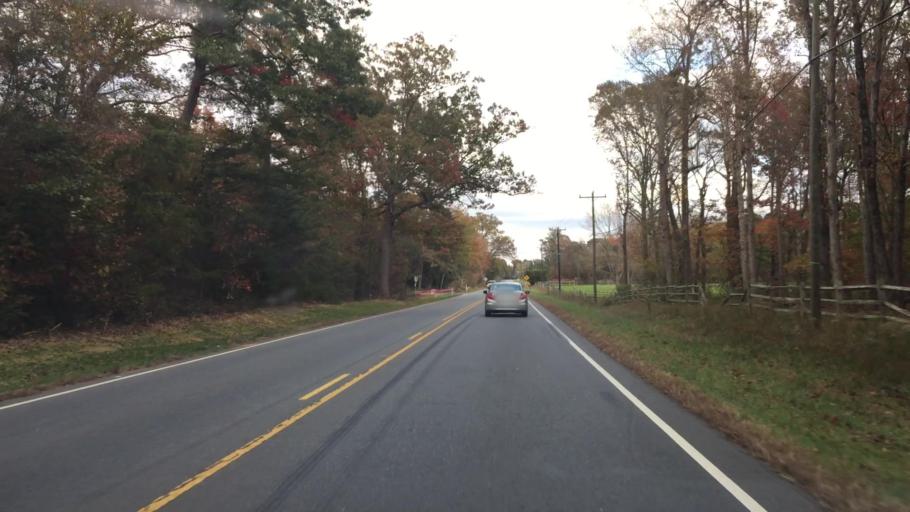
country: US
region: North Carolina
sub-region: Guilford County
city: Summerfield
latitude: 36.2551
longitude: -79.8879
